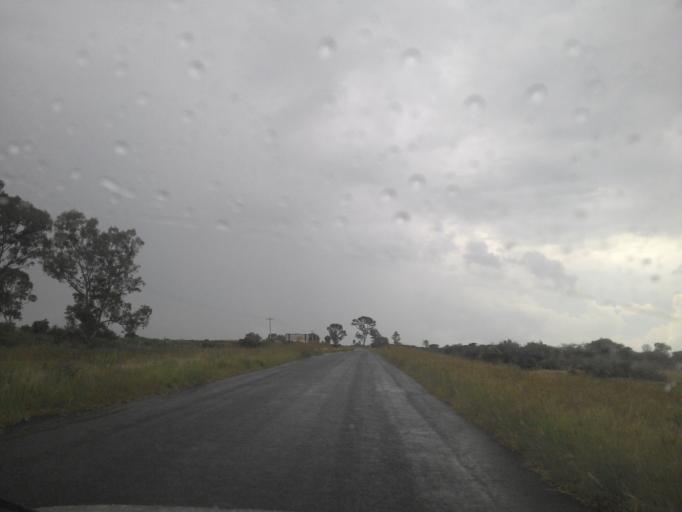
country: MX
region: Jalisco
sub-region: Arandas
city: Santiaguito (Santiaguito de Velazquez)
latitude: 20.8121
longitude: -102.2109
